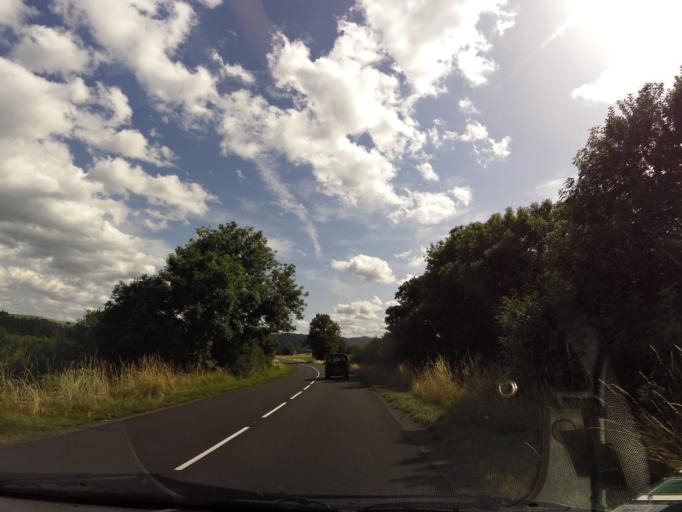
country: FR
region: Auvergne
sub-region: Departement du Puy-de-Dome
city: Aydat
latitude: 45.5320
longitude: 2.9466
